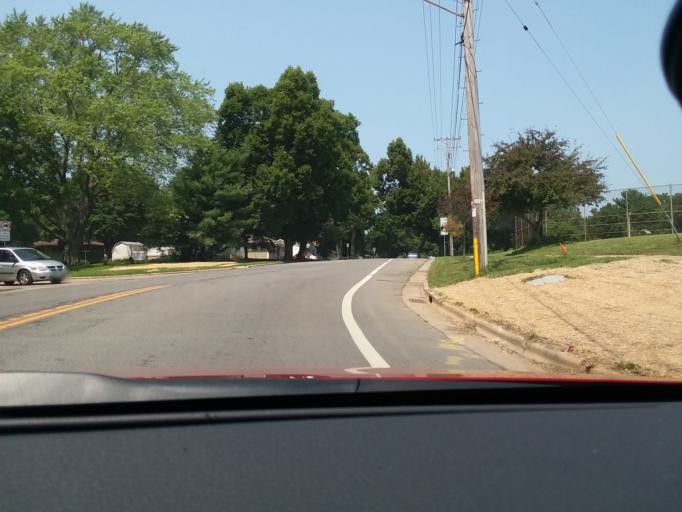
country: US
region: Wisconsin
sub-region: Dane County
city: Monona
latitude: 43.1139
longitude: -89.3149
